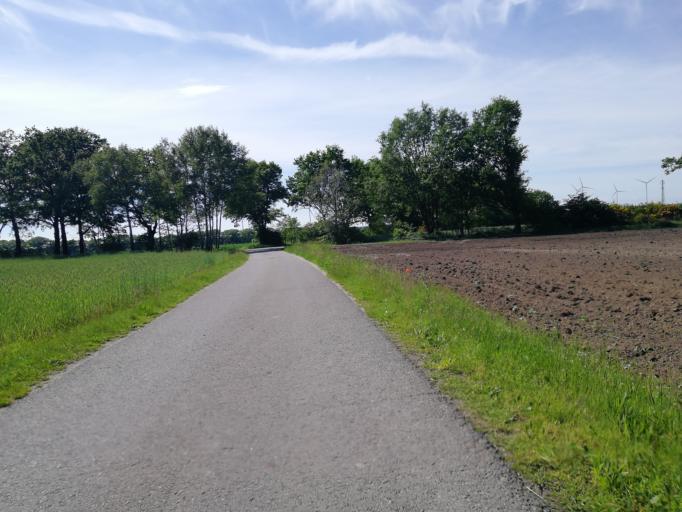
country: DE
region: Brandenburg
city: Calau
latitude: 51.7242
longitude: 13.9209
